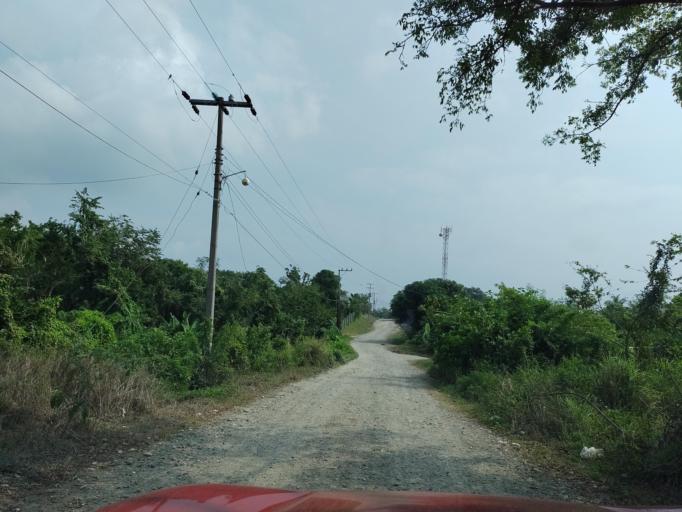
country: MX
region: Veracruz
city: Agua Dulce
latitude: 20.3634
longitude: -97.2990
